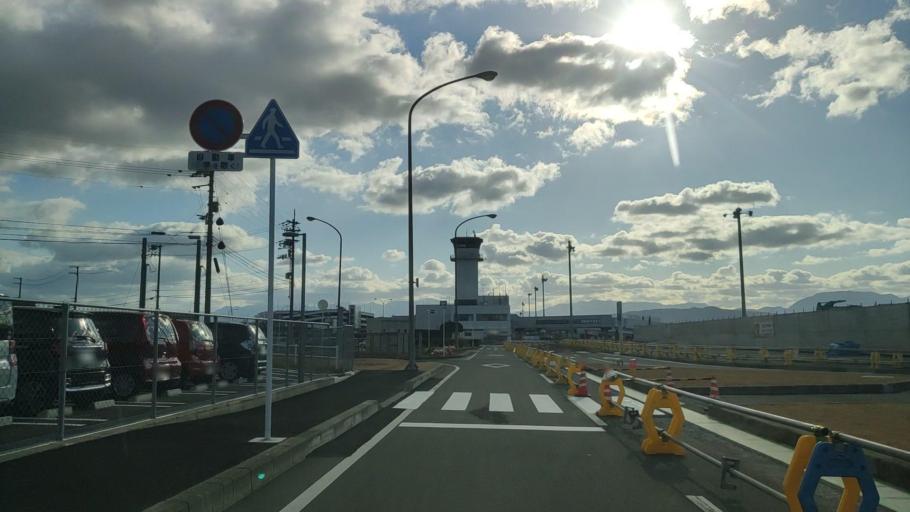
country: JP
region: Ehime
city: Masaki-cho
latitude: 33.8310
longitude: 132.7010
